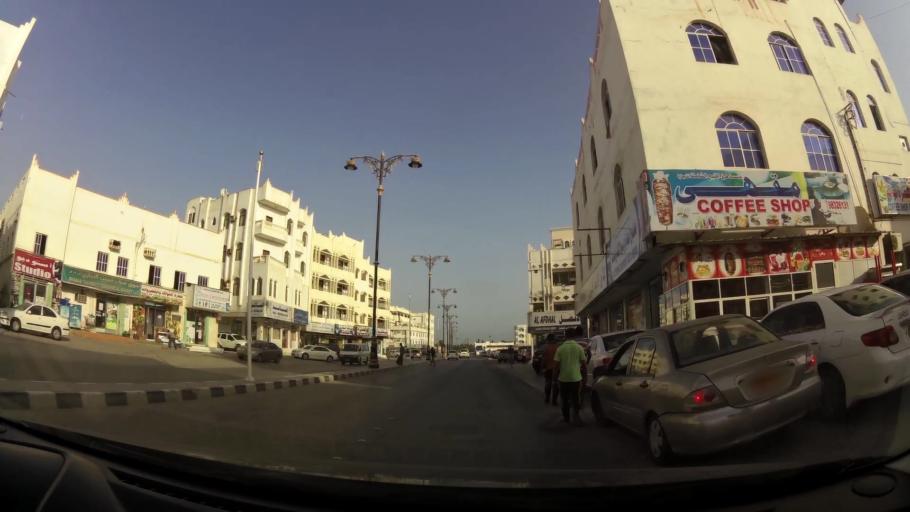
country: OM
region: Zufar
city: Salalah
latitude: 17.0119
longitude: 54.0940
